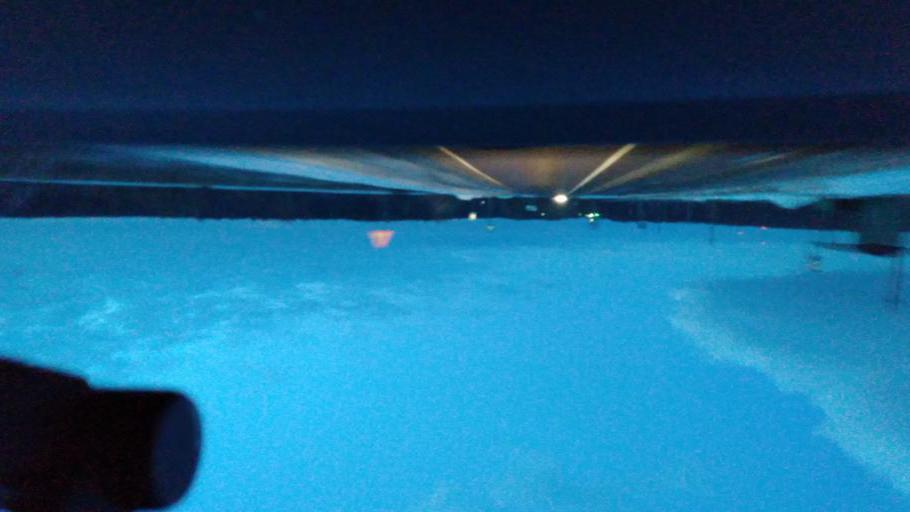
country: RU
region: Moskovskaya
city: Krasnaya Poyma
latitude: 55.1852
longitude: 39.1226
